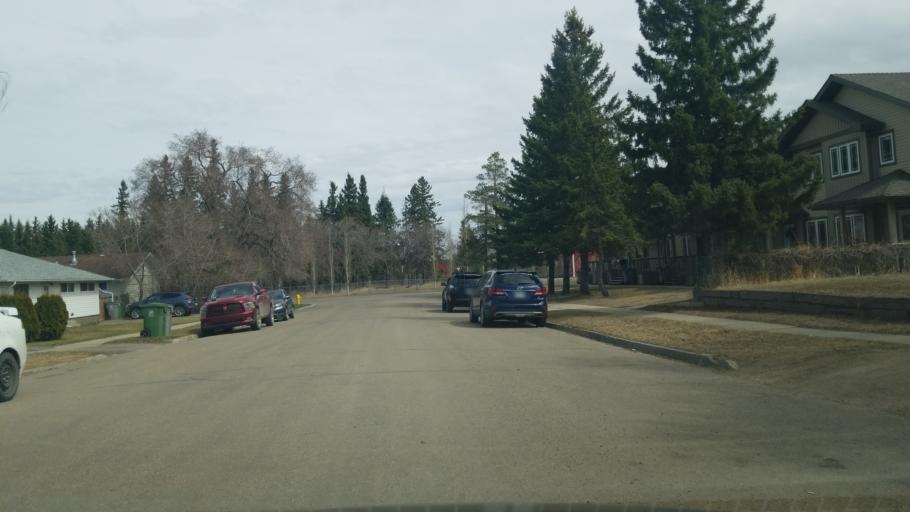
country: CA
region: Saskatchewan
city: Lloydminster
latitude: 53.2771
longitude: -109.9986
